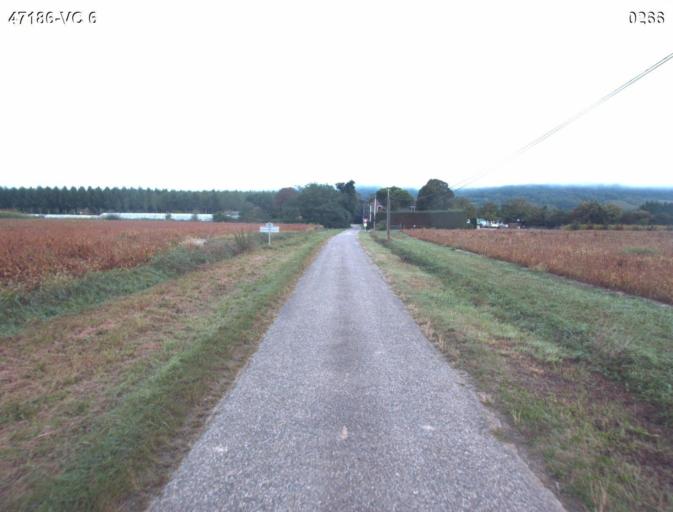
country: FR
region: Aquitaine
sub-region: Departement du Lot-et-Garonne
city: Port-Sainte-Marie
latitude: 44.2305
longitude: 0.4447
